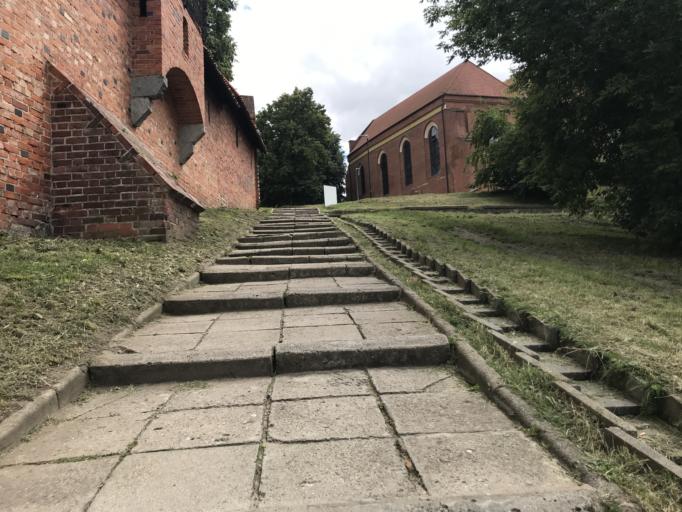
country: PL
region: Pomeranian Voivodeship
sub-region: Powiat malborski
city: Malbork
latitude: 54.0392
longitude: 19.0258
